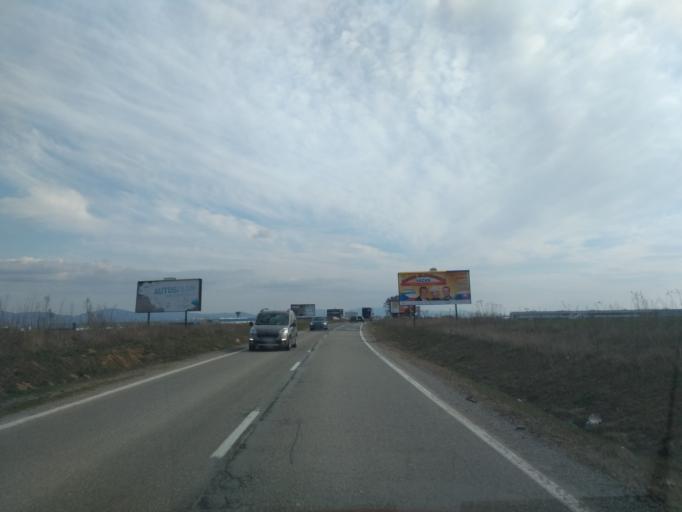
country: SK
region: Kosicky
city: Kosice
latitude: 48.6848
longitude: 21.2293
